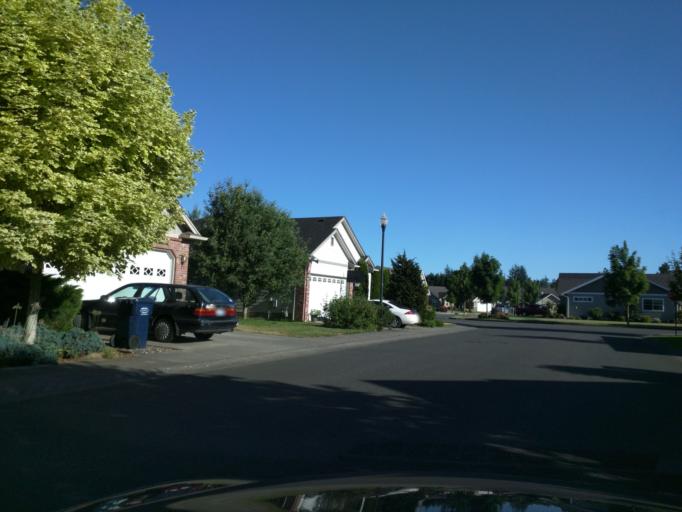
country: US
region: Washington
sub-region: Whatcom County
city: Lynden
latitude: 48.9560
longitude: -122.4508
